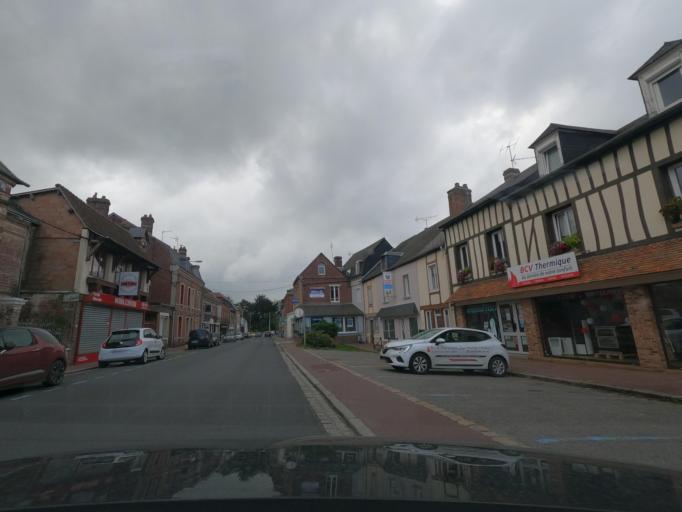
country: FR
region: Haute-Normandie
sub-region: Departement de la Seine-Maritime
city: Forges-les-Eaux
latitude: 49.6125
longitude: 1.5474
